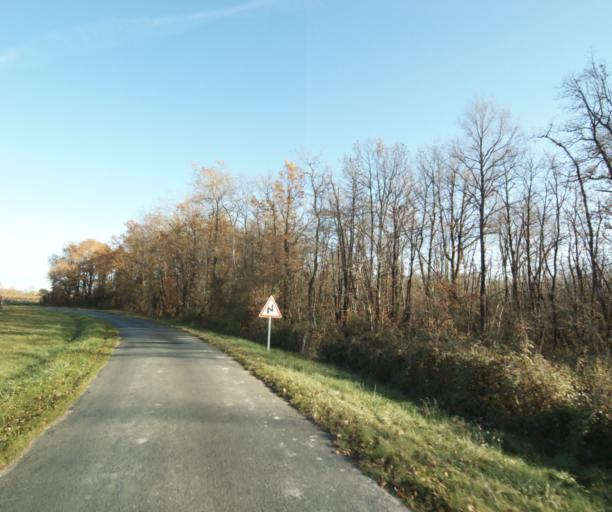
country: FR
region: Poitou-Charentes
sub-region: Departement de la Charente-Maritime
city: Burie
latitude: 45.7765
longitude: -0.4474
